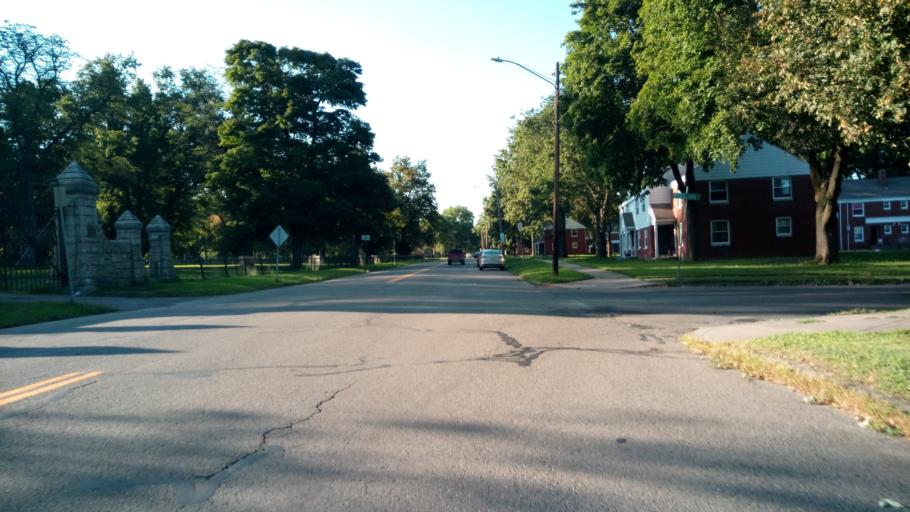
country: US
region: New York
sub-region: Chemung County
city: Elmira Heights
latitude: 42.1079
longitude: -76.8248
